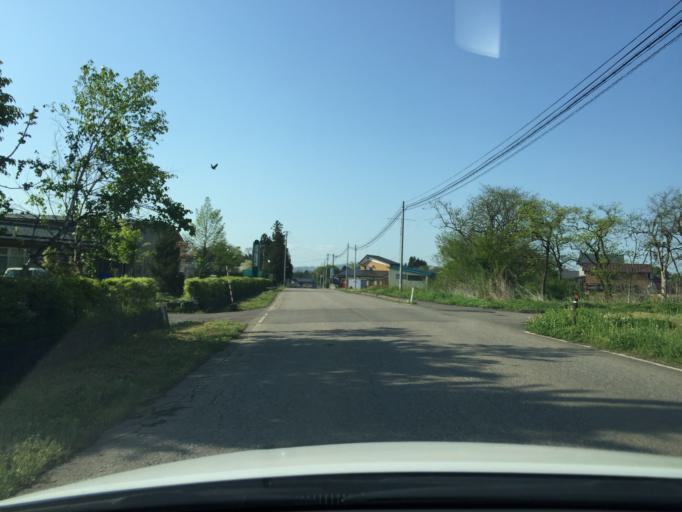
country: JP
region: Fukushima
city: Kitakata
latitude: 37.6552
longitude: 139.7745
